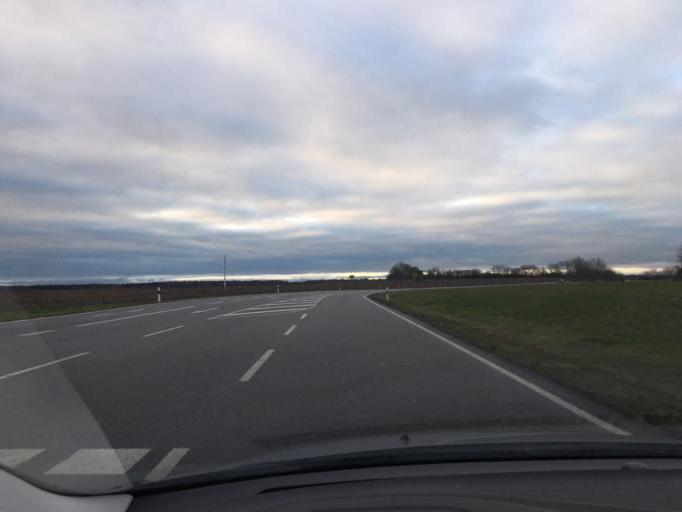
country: DE
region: Saxony
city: Frohburg
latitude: 51.0471
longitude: 12.5568
